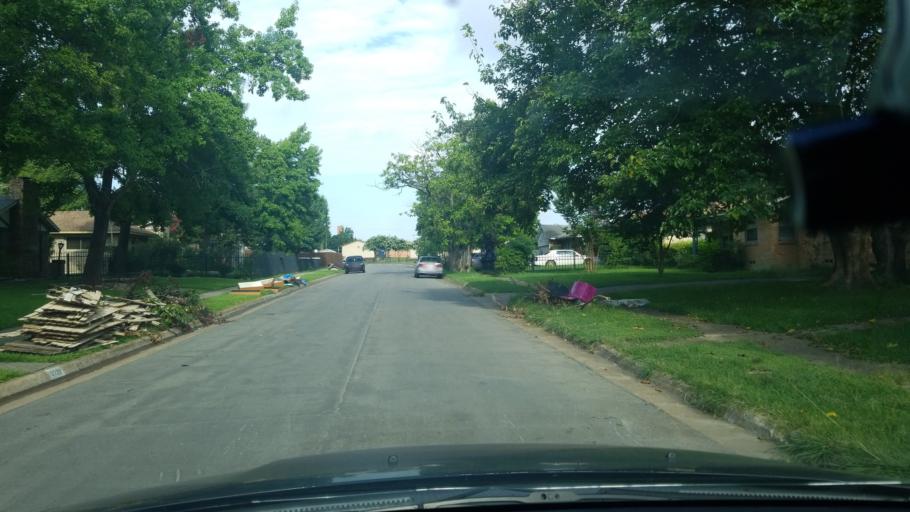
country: US
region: Texas
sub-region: Dallas County
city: Balch Springs
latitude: 32.7515
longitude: -96.6661
